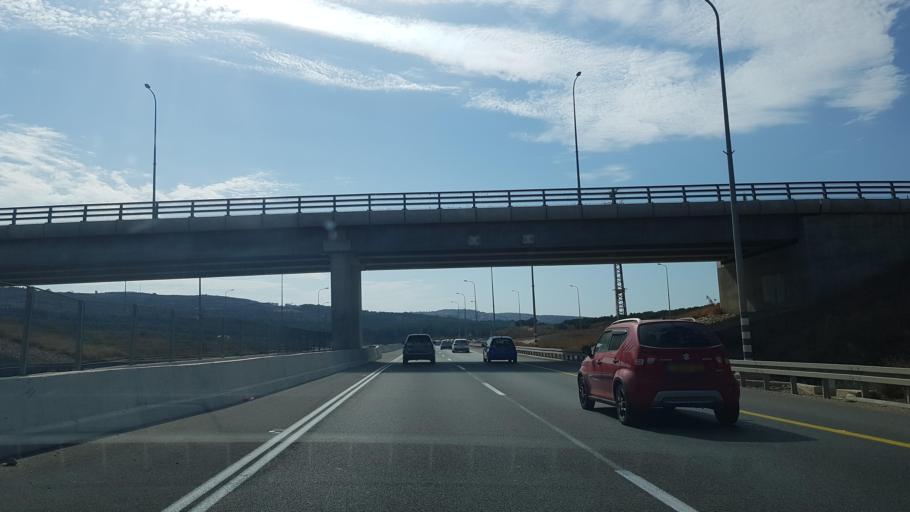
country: IL
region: Northern District
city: Kafr Kanna
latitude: 32.7645
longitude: 35.3767
